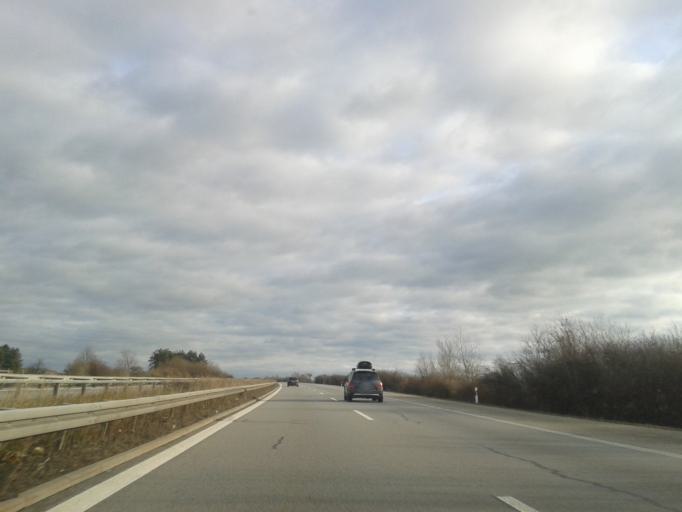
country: DE
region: Saxony
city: Weissenberg
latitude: 51.2084
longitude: 14.6014
